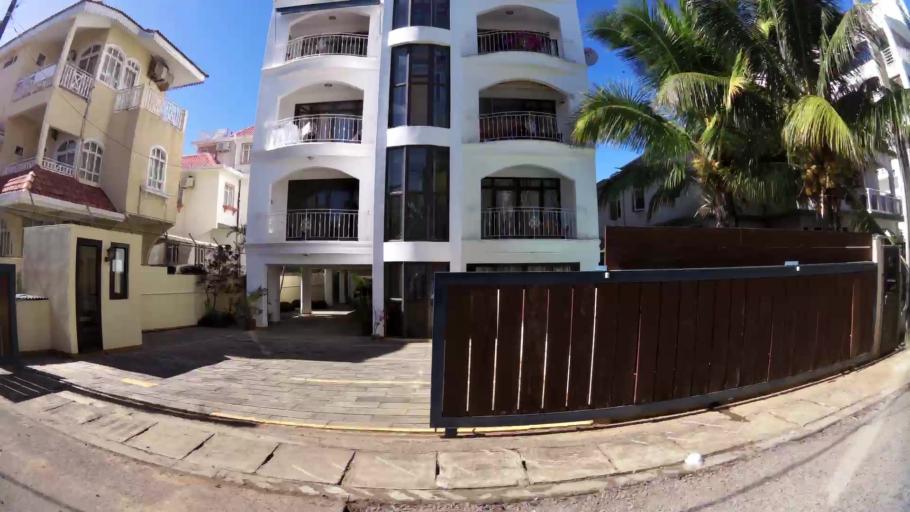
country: MU
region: Black River
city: Flic en Flac
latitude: -20.2783
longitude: 57.3693
